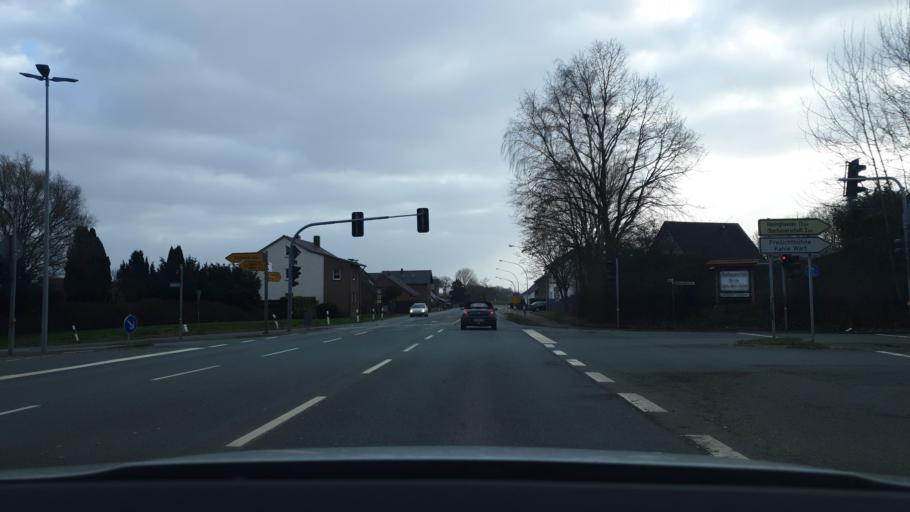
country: DE
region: North Rhine-Westphalia
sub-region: Regierungsbezirk Detmold
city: Huellhorst
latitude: 52.2781
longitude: 8.6337
